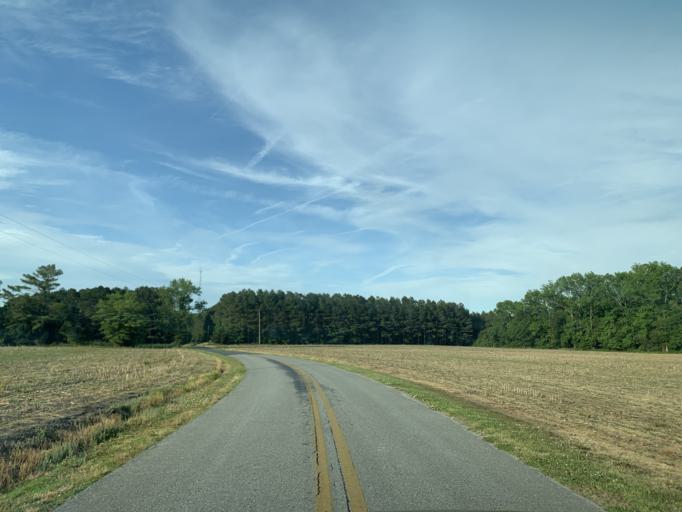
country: US
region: Maryland
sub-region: Worcester County
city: Pocomoke City
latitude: 38.0830
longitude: -75.4698
